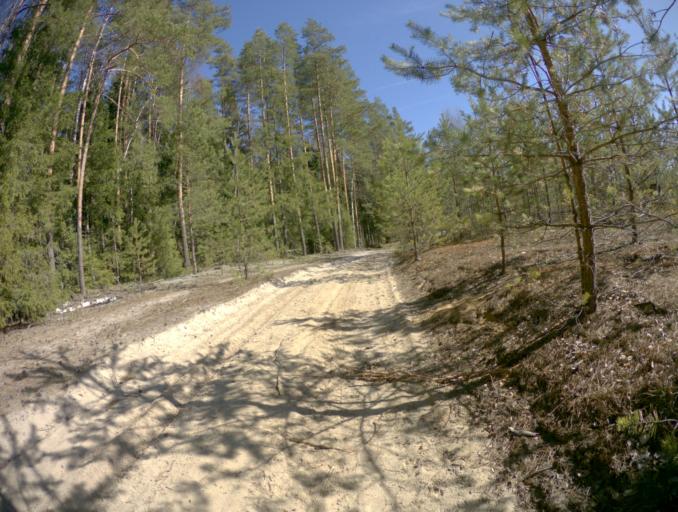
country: RU
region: Vladimir
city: Ivanishchi
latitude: 55.8020
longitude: 40.4221
